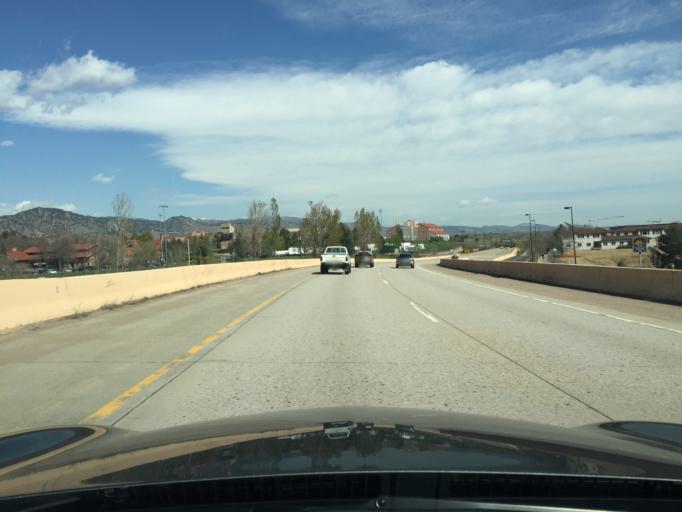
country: US
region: Colorado
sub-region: Boulder County
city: Boulder
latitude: 40.0008
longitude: -105.2582
